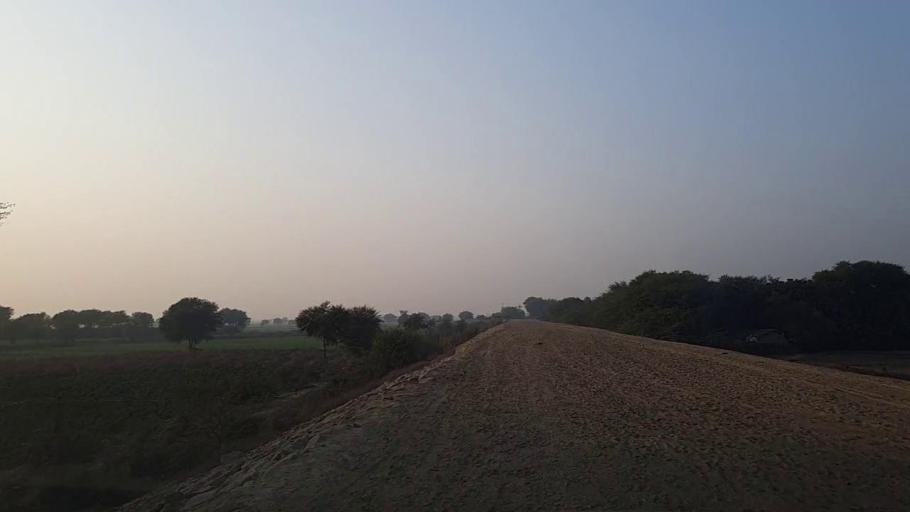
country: PK
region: Sindh
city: Sann
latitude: 26.1760
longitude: 68.0989
